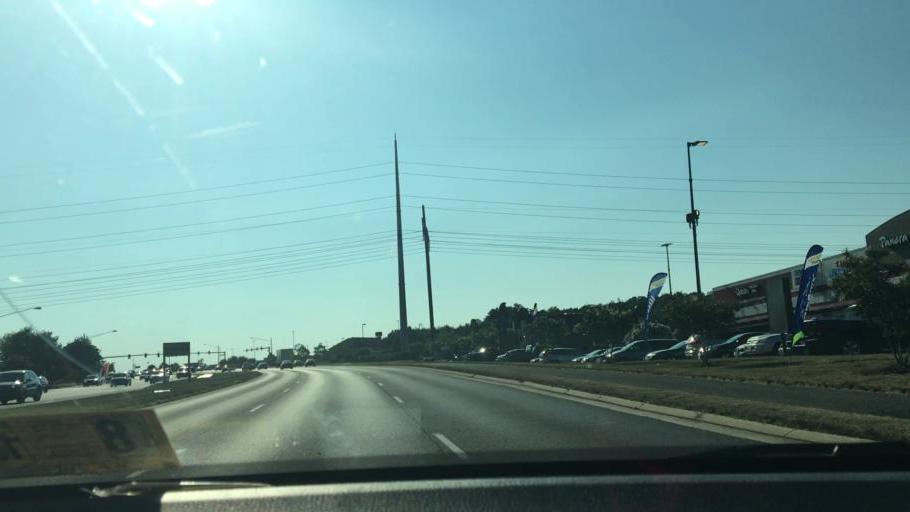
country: US
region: Virginia
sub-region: Prince William County
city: Potomac Mills
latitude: 38.6514
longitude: -77.2956
